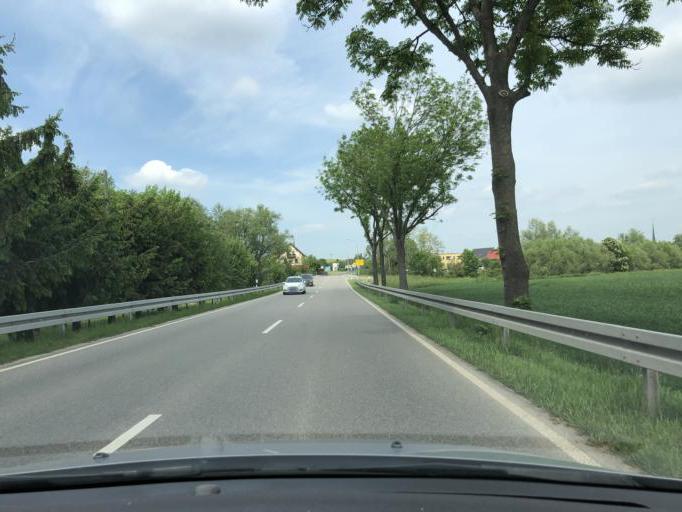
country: DE
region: Thuringia
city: Saara
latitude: 50.9486
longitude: 12.4255
